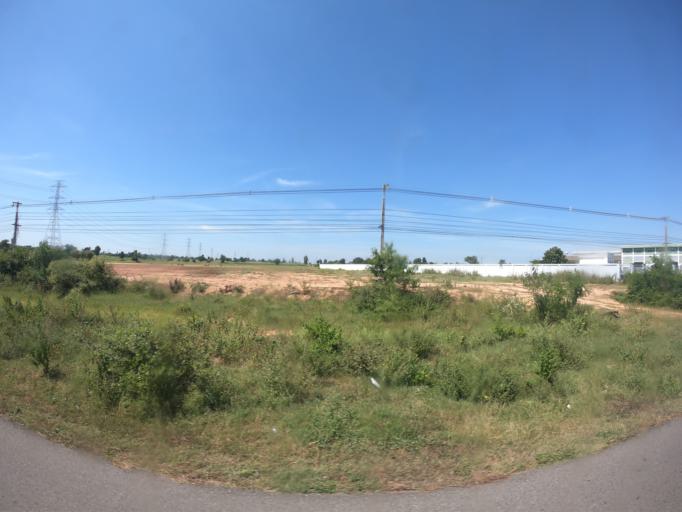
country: TH
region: Khon Kaen
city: Non Sila
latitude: 15.9426
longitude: 102.6782
